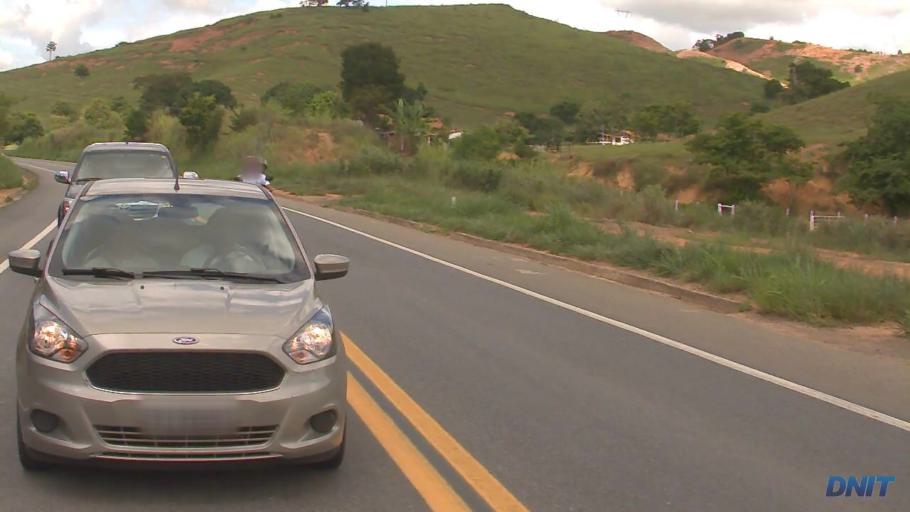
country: BR
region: Minas Gerais
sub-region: Governador Valadares
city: Governador Valadares
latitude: -18.9629
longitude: -42.0778
